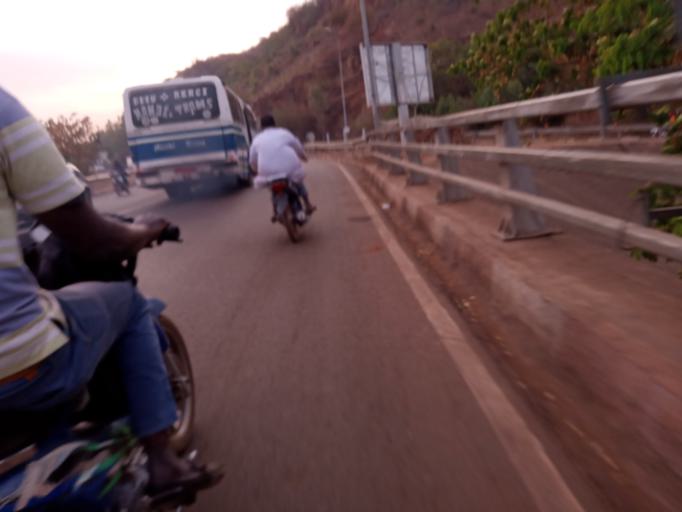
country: ML
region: Bamako
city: Bamako
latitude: 12.6576
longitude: -8.0003
